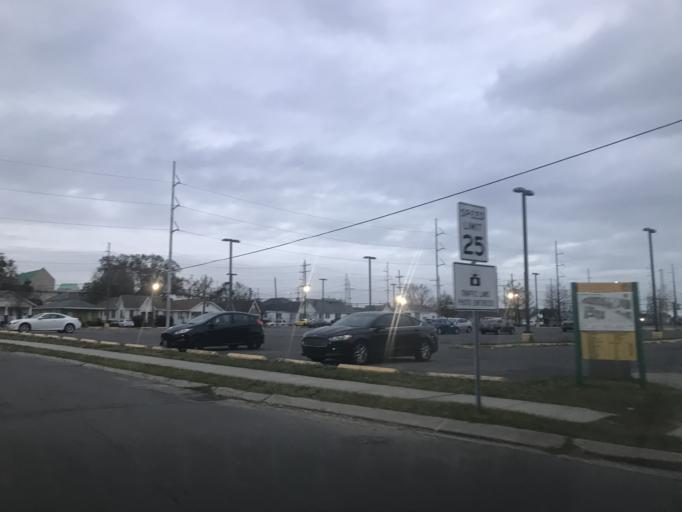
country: US
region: Louisiana
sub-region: Orleans Parish
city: New Orleans
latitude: 29.9614
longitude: -90.1033
